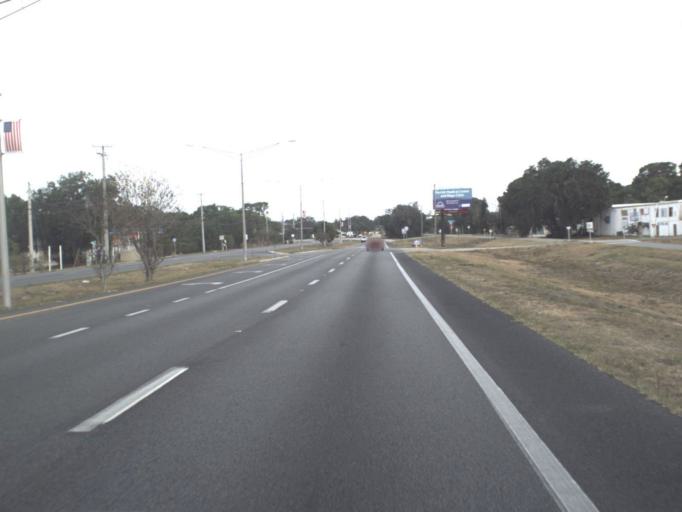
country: US
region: Florida
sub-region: Brevard County
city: Titusville
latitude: 28.6253
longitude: -80.8229
